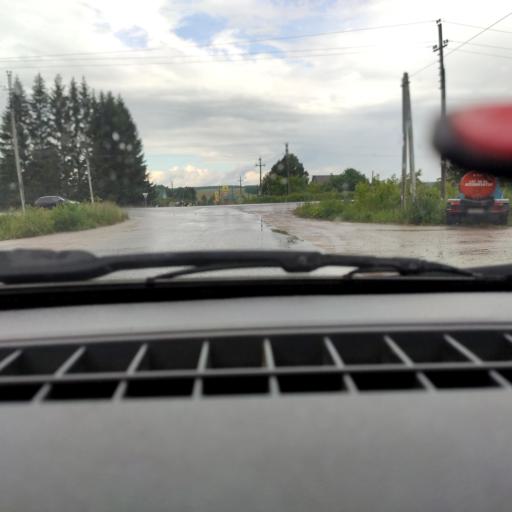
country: RU
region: Bashkortostan
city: Kabakovo
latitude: 54.5812
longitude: 56.2789
